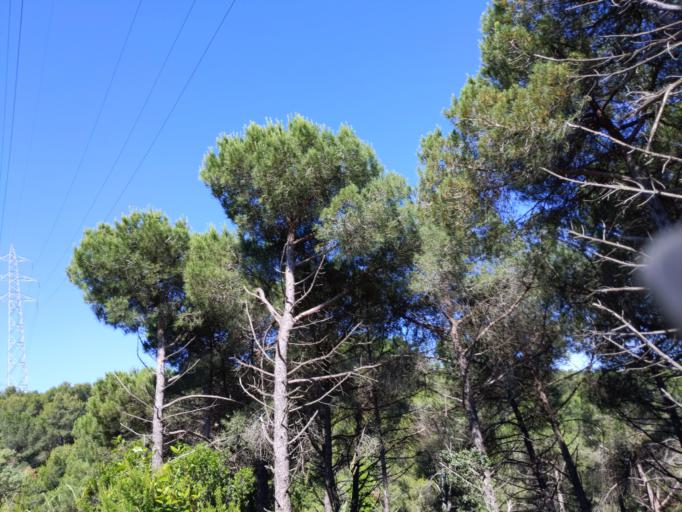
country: ES
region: Catalonia
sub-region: Provincia de Barcelona
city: Nou Barris
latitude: 41.4480
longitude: 2.1526
